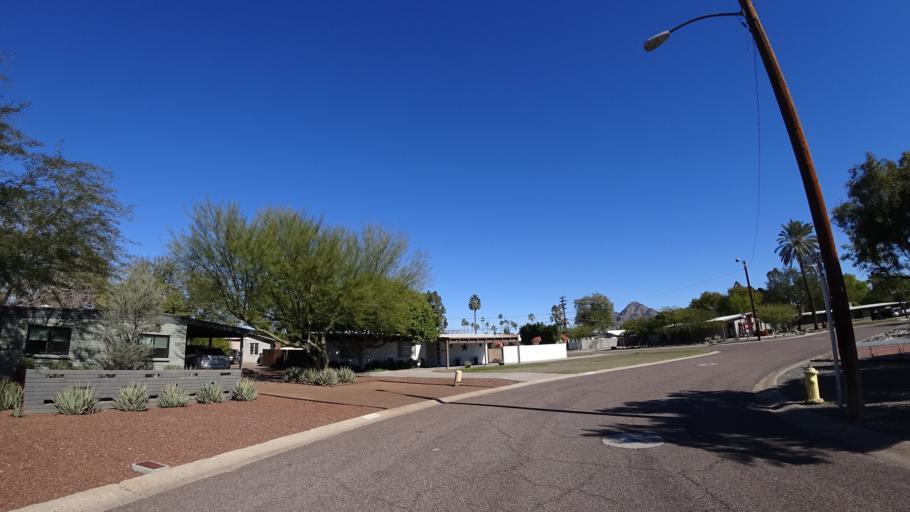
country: US
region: Arizona
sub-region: Maricopa County
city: Phoenix
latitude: 33.5228
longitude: -112.0598
